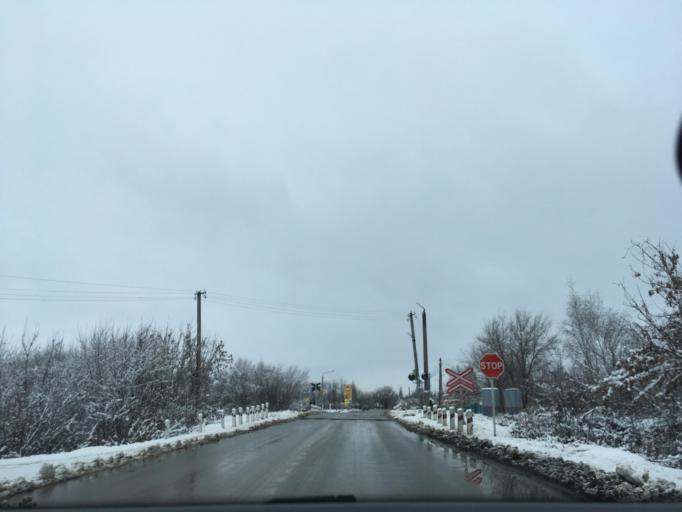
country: RU
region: Voronezj
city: Ol'khovatka
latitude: 50.2590
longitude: 39.2905
